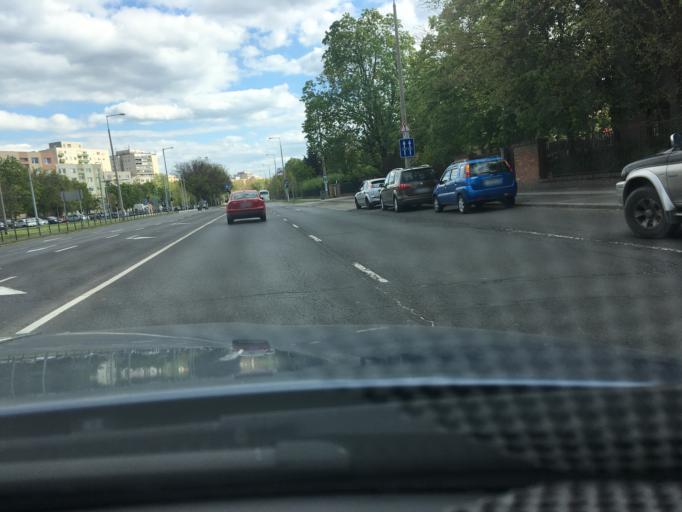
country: HU
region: Hajdu-Bihar
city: Debrecen
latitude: 47.5557
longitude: 21.6068
